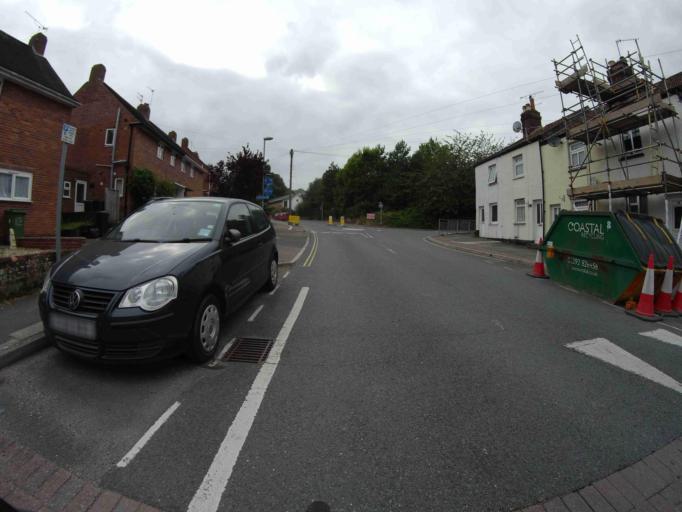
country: GB
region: England
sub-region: Devon
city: Heavitree
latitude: 50.7150
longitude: -3.5010
